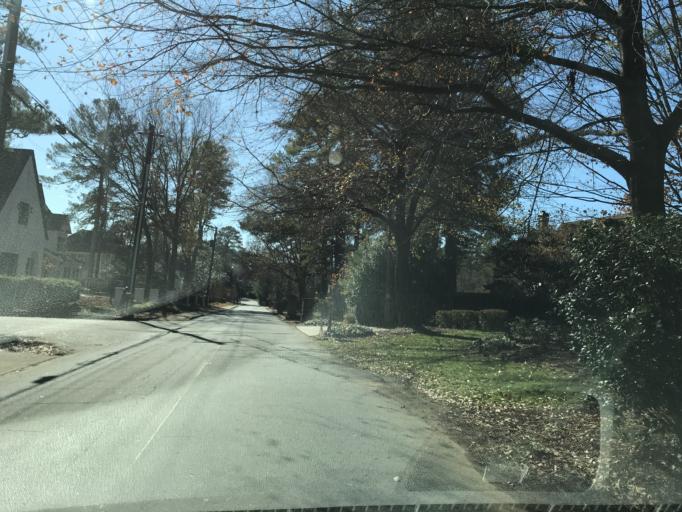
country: US
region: Georgia
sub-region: DeKalb County
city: North Atlanta
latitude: 33.8802
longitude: -84.3467
